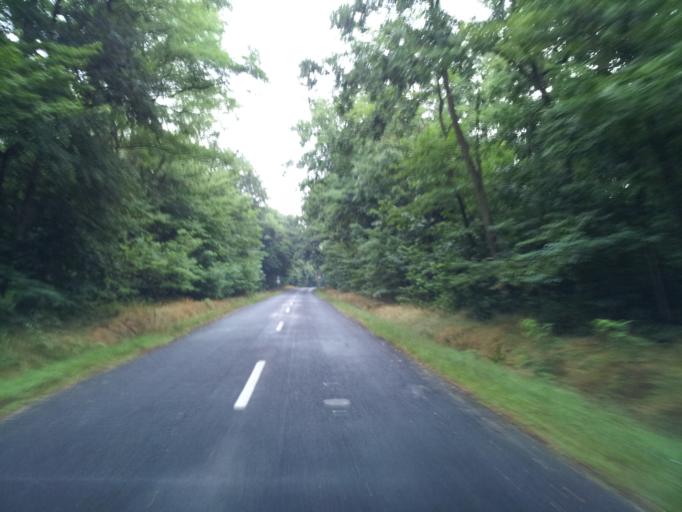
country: HU
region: Vas
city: Kormend
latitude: 46.9489
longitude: 16.5822
